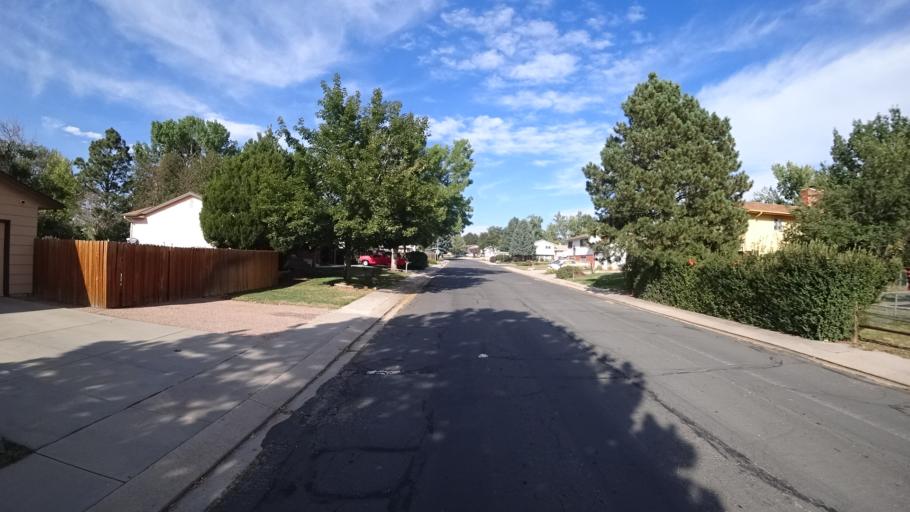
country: US
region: Colorado
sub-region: El Paso County
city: Cimarron Hills
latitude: 38.8965
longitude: -104.7668
